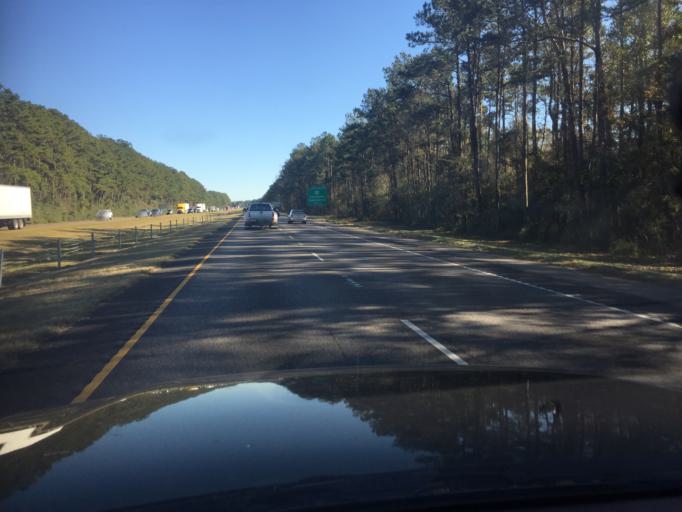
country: US
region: Louisiana
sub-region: Saint Tammany Parish
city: Covington
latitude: 30.4364
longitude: -90.1091
